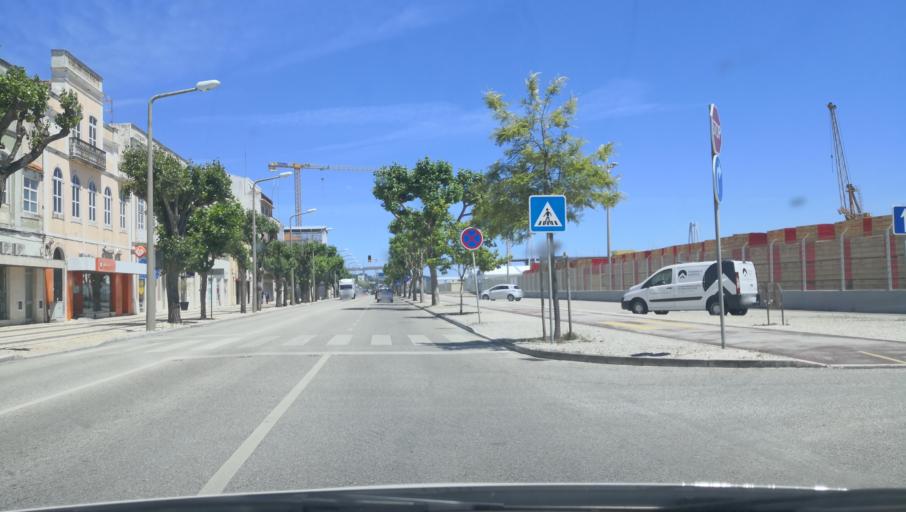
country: PT
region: Coimbra
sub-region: Figueira da Foz
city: Figueira da Foz
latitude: 40.1480
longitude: -8.8533
